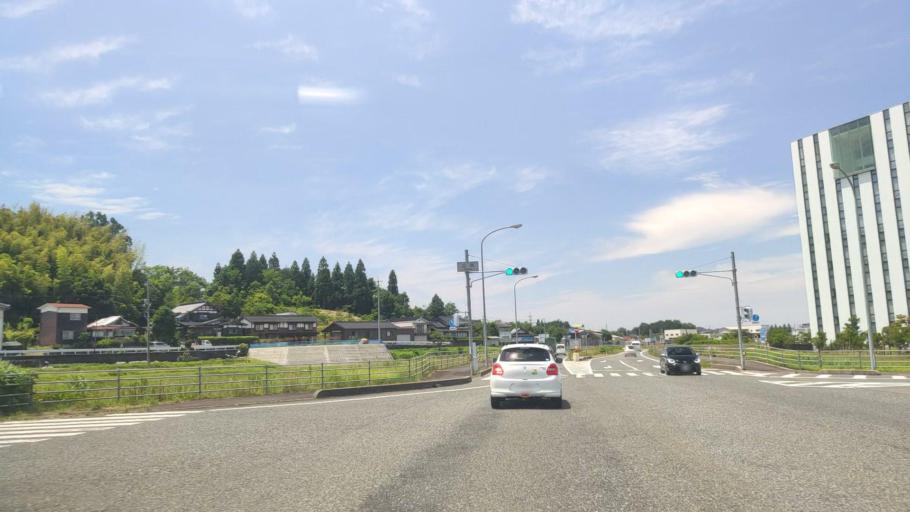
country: JP
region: Tottori
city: Tottori
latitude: 35.4510
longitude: 134.2480
